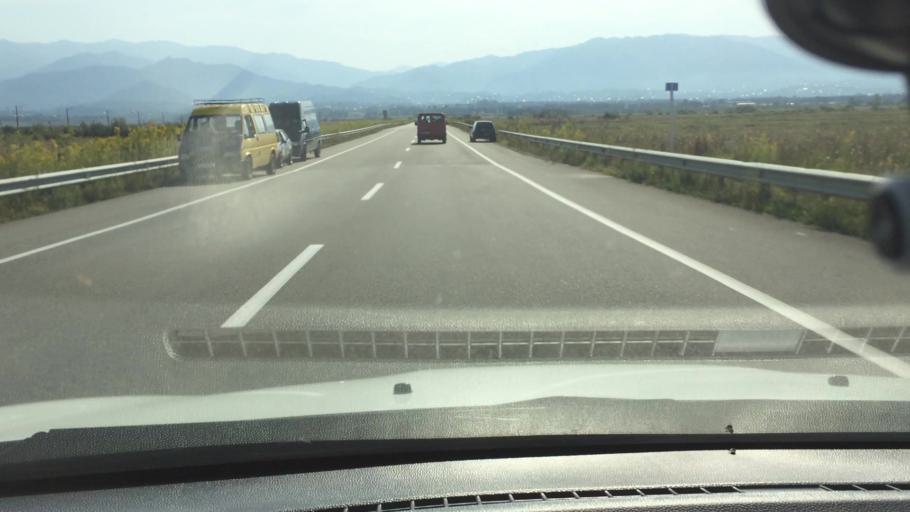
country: GE
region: Ajaria
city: Ochkhamuri
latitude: 41.8779
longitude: 41.8225
